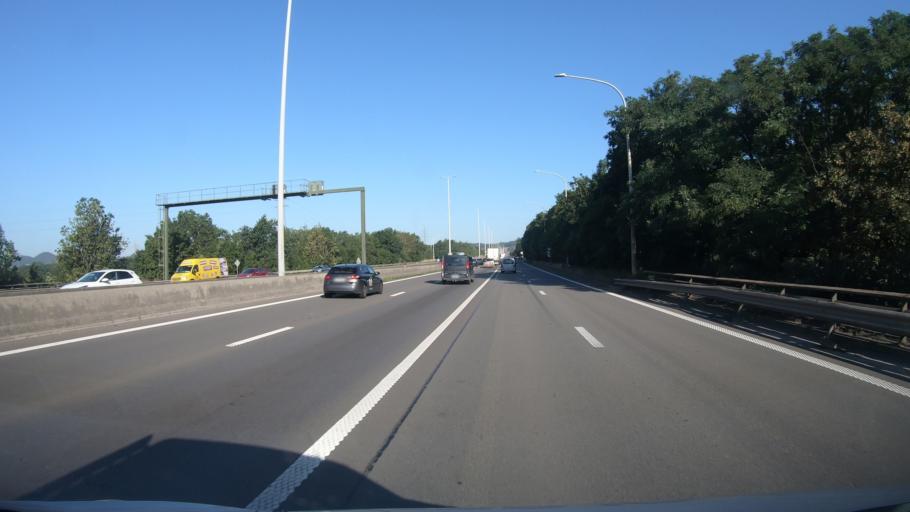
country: BE
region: Wallonia
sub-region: Province de Liege
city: Oupeye
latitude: 50.6790
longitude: 5.6649
